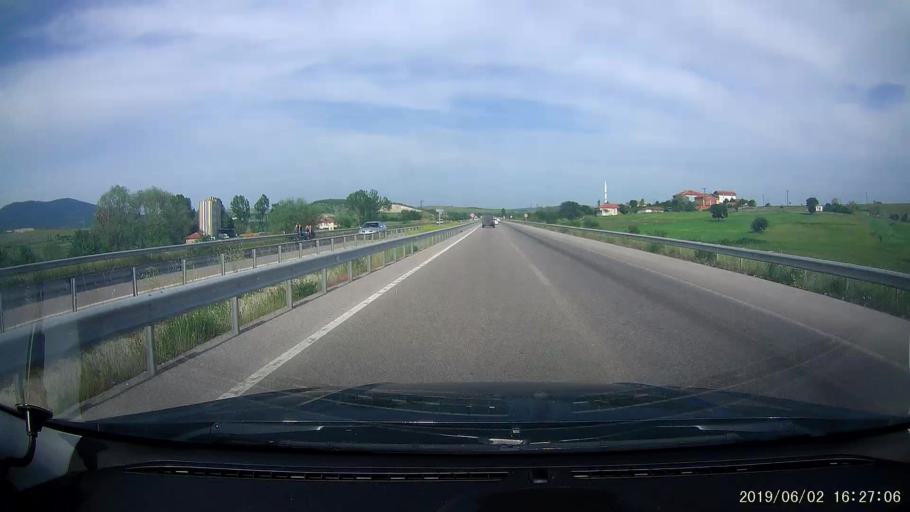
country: TR
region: Samsun
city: Ladik
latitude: 41.0016
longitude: 35.8194
